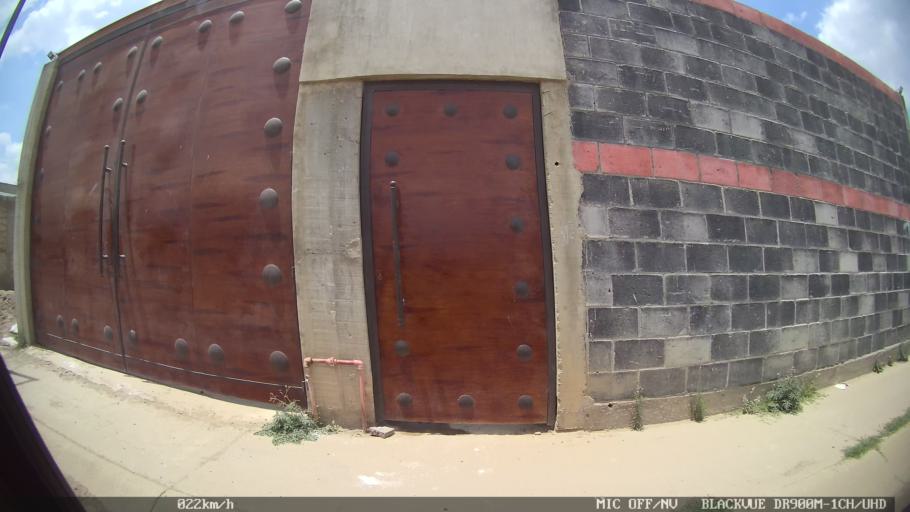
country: MX
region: Jalisco
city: Coyula
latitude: 20.6657
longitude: -103.2261
